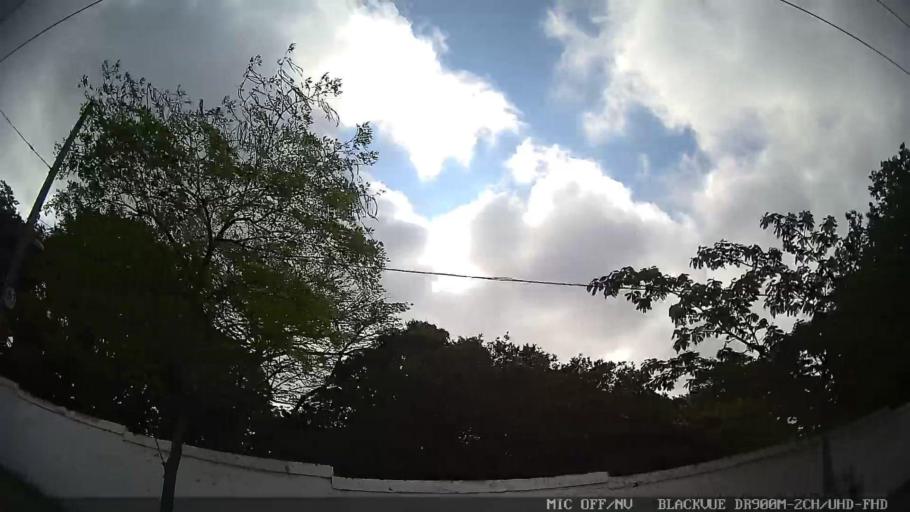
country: BR
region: Sao Paulo
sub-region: Sao Caetano Do Sul
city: Sao Caetano do Sul
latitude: -23.5623
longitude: -46.5224
